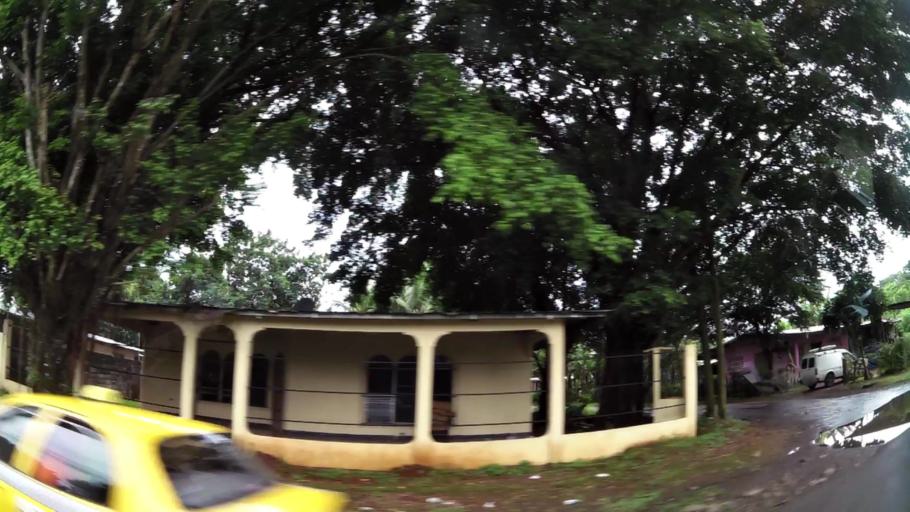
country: PA
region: Chiriqui
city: David
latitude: 8.4188
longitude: -82.4435
